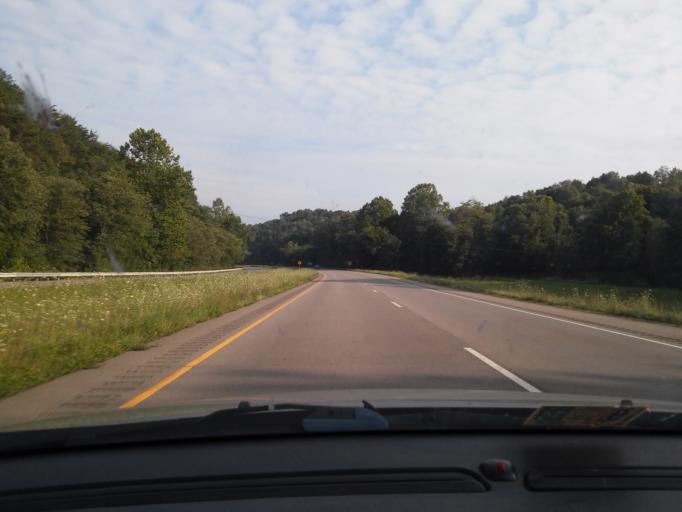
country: US
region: Ohio
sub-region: Jackson County
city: Oak Hill
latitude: 38.9292
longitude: -82.4672
